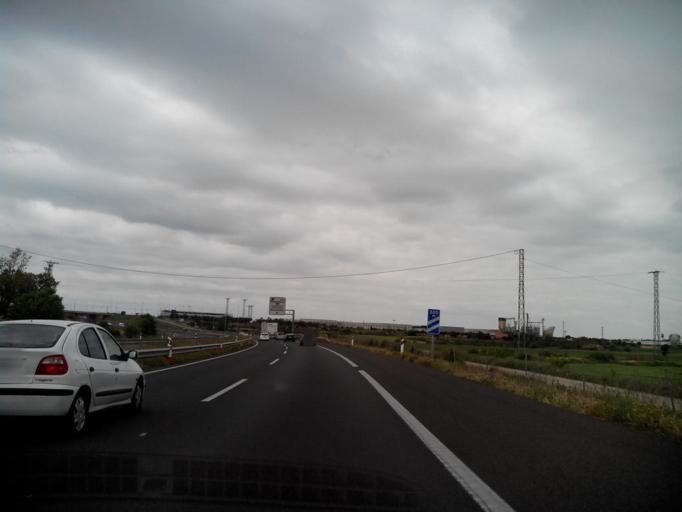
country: ES
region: Catalonia
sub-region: Provincia de Lleida
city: Anglesola
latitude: 41.6569
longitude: 1.1028
